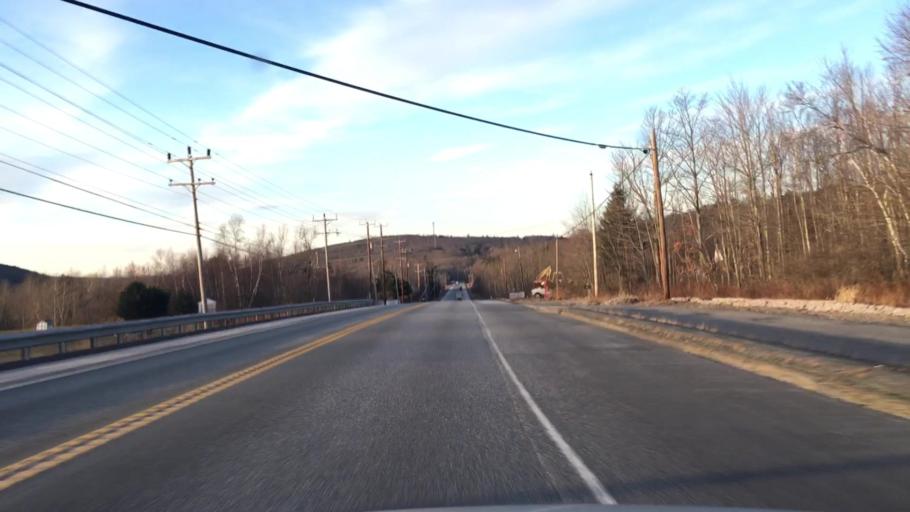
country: US
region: Maine
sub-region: Hancock County
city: Dedham
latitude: 44.7049
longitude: -68.5997
